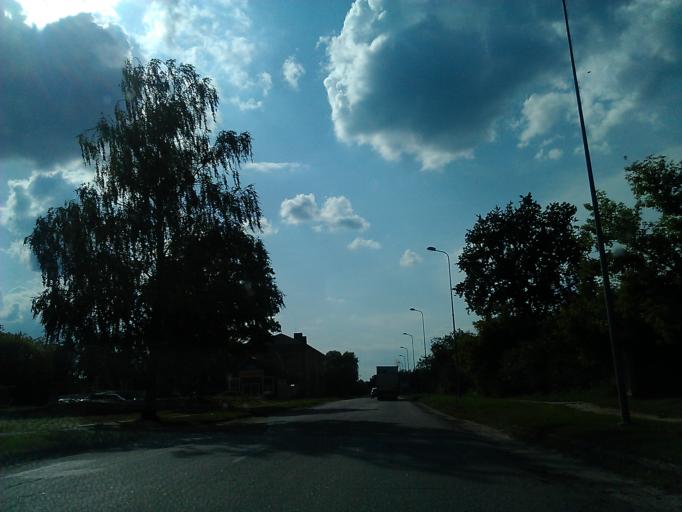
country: LV
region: Skrunda
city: Skrunda
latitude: 56.6729
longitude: 22.0223
